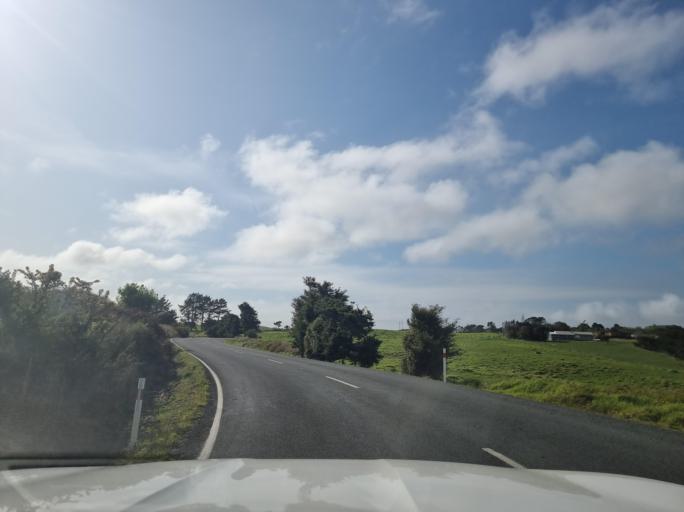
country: NZ
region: Northland
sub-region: Whangarei
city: Ruakaka
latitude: -36.0103
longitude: 174.4594
